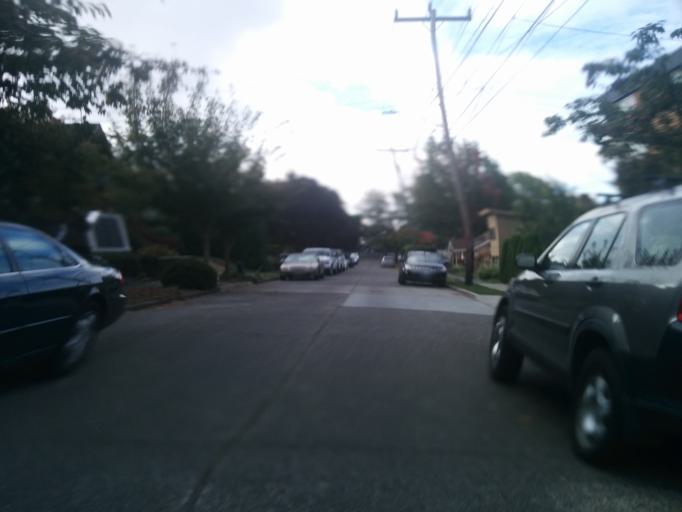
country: US
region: Washington
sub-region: King County
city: Shoreline
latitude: 47.6843
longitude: -122.3143
